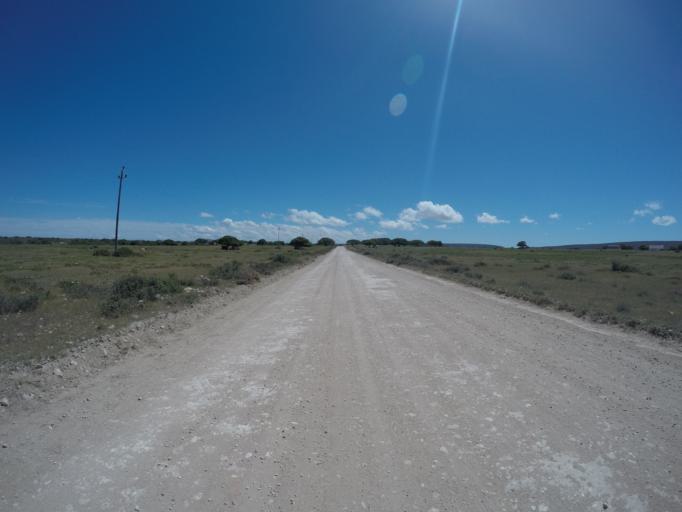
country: ZA
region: Western Cape
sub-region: Overberg District Municipality
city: Bredasdorp
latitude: -34.4559
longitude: 20.4042
